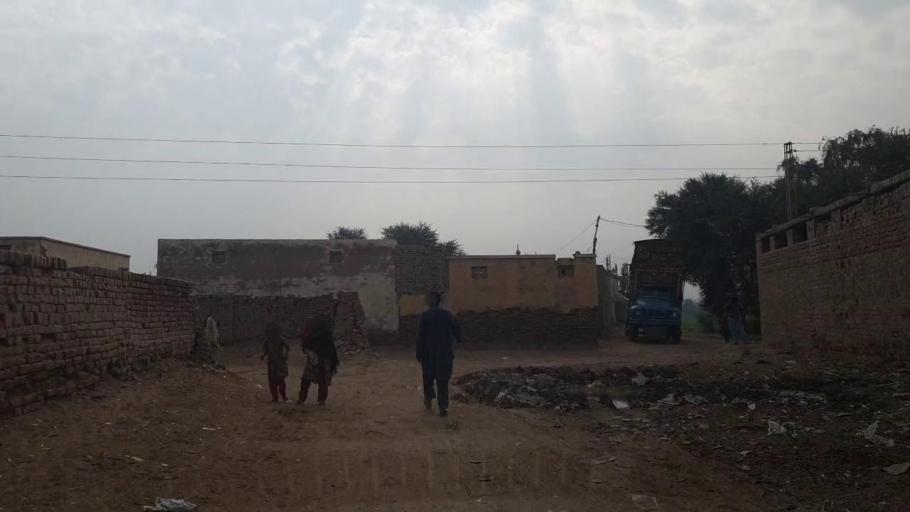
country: PK
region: Sindh
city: Sann
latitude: 25.9964
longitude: 68.1848
